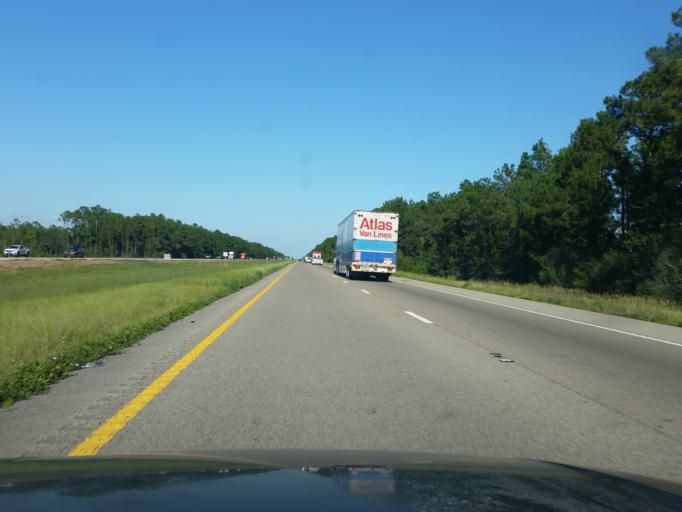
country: US
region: Mississippi
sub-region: Hancock County
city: Kiln
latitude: 30.3483
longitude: -89.4551
